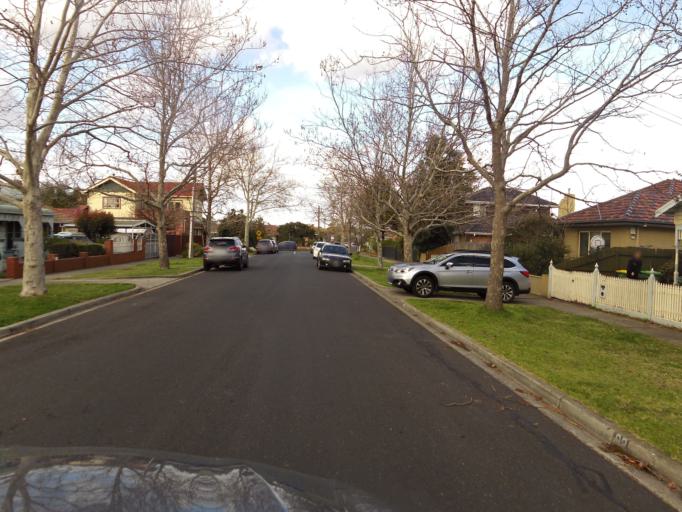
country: AU
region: Victoria
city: Spotswood
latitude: -37.8197
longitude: 144.8846
